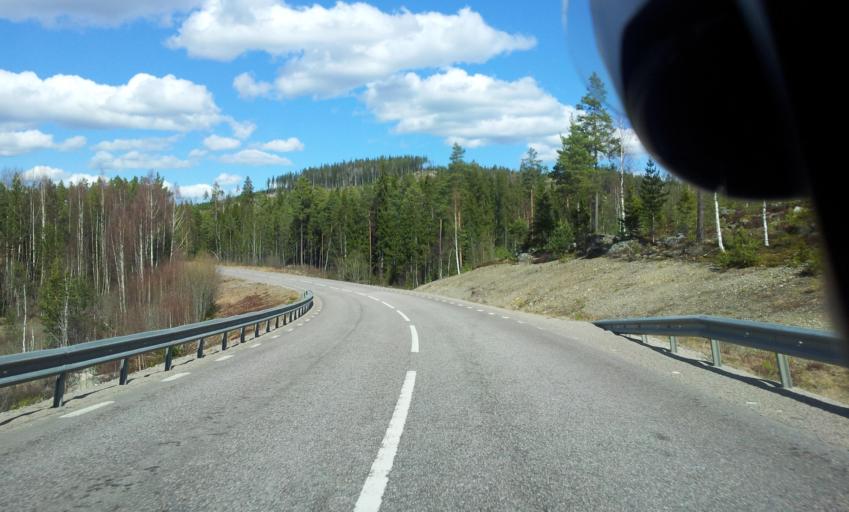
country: SE
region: Gaevleborg
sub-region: Ovanakers Kommun
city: Edsbyn
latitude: 61.2287
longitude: 15.8829
